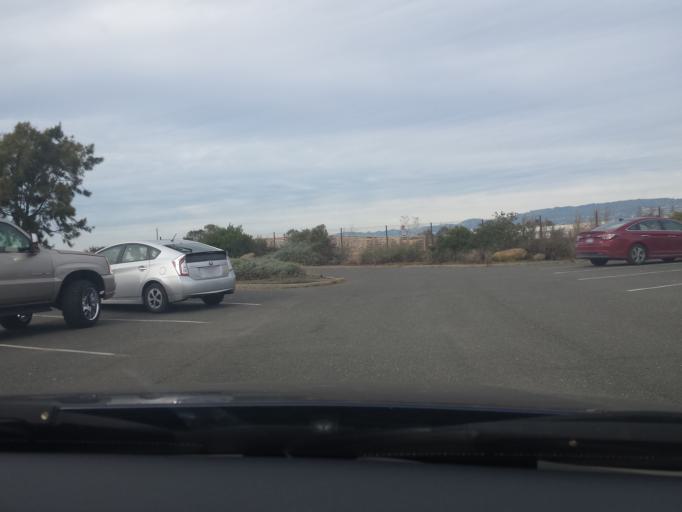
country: US
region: California
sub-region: Alameda County
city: Alameda
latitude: 37.7420
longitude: -122.2089
